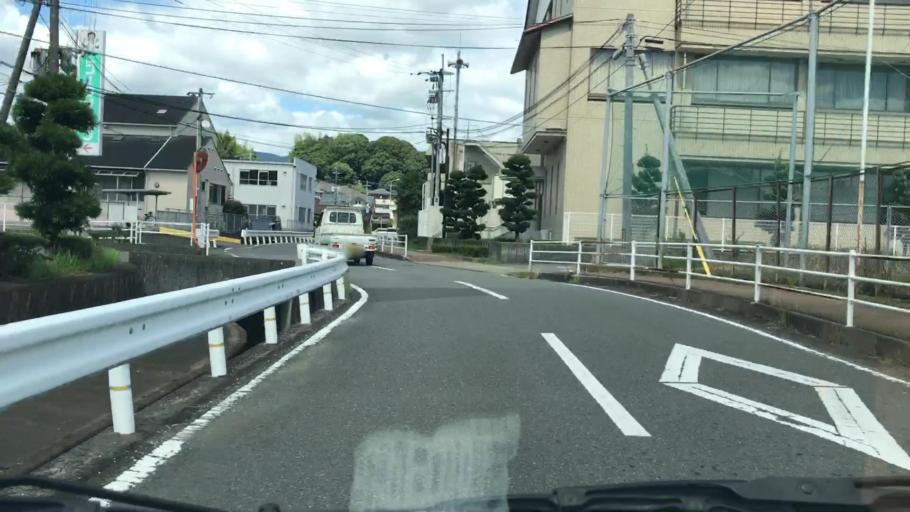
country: JP
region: Saga Prefecture
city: Takeocho-takeo
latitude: 33.2191
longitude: 130.0683
